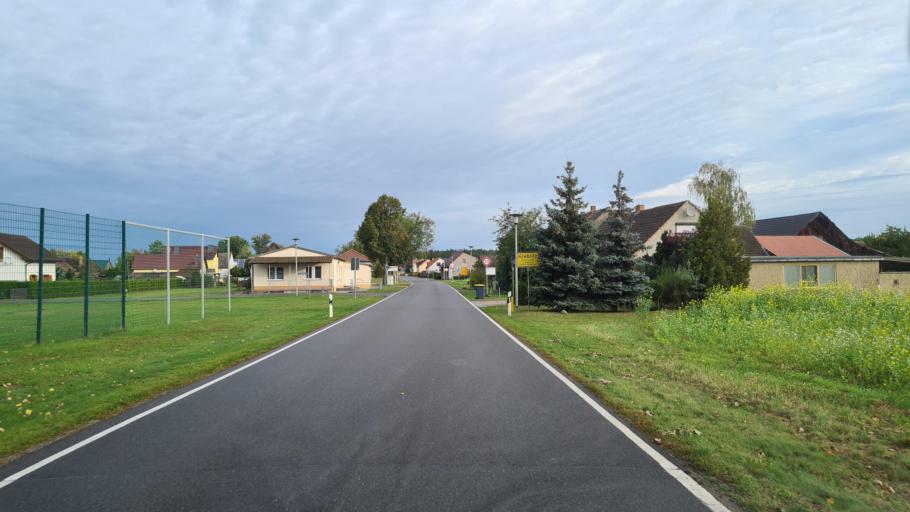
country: DE
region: Brandenburg
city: Kasel-Golzig
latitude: 51.9003
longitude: 13.7153
